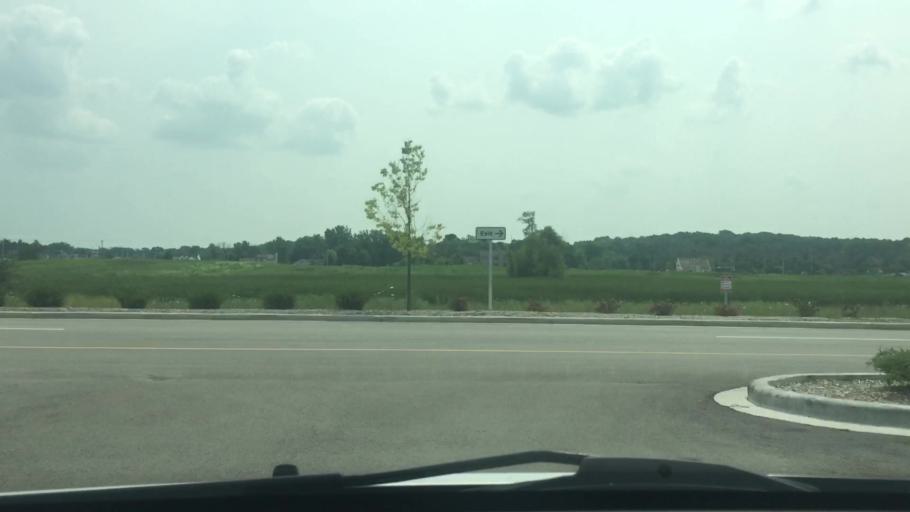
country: US
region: Wisconsin
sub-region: Milwaukee County
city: Greendale
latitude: 42.9060
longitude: -87.9391
